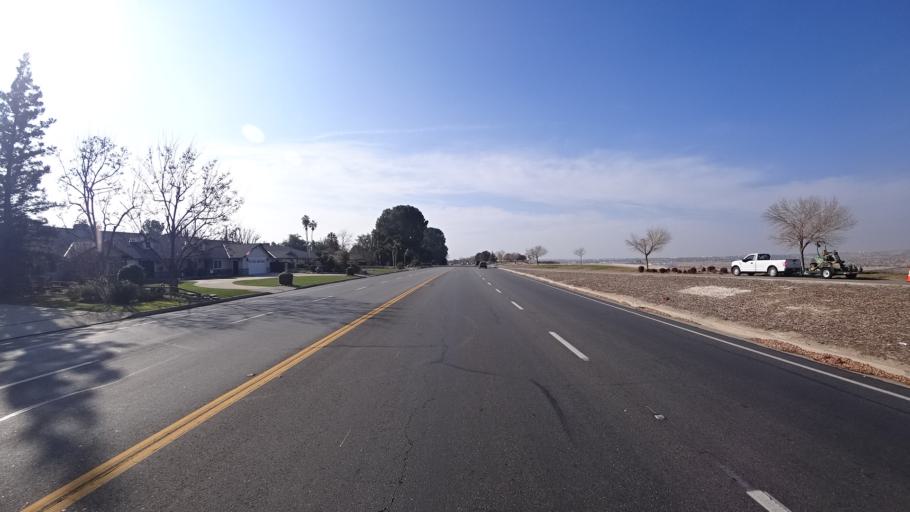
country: US
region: California
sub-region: Kern County
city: Oildale
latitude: 35.4100
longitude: -118.9777
